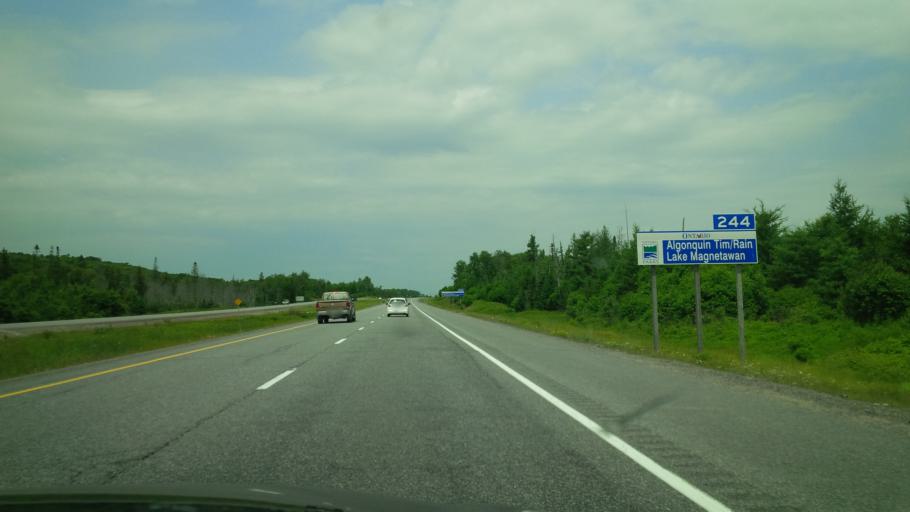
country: CA
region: Ontario
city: Huntsville
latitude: 45.4902
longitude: -79.2866
